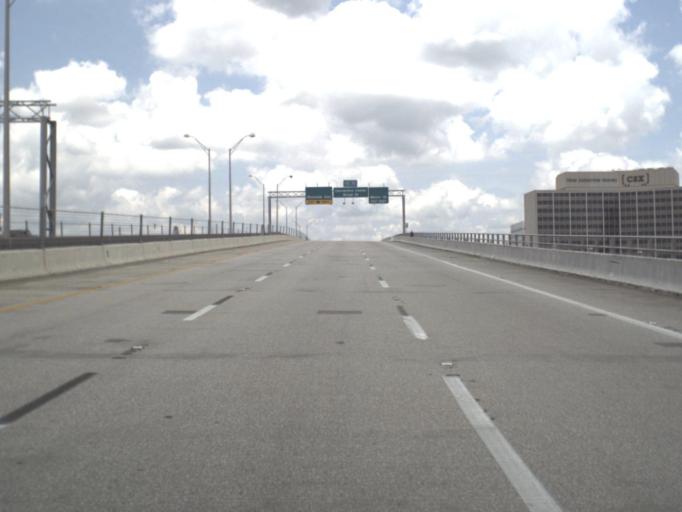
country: US
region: Florida
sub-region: Duval County
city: Jacksonville
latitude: 30.3198
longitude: -81.6627
